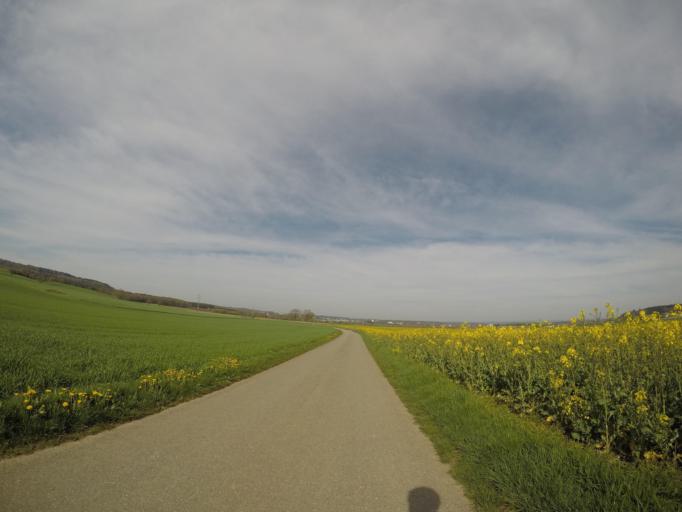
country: DE
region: Baden-Wuerttemberg
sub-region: Tuebingen Region
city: Boms
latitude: 48.0073
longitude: 9.5475
